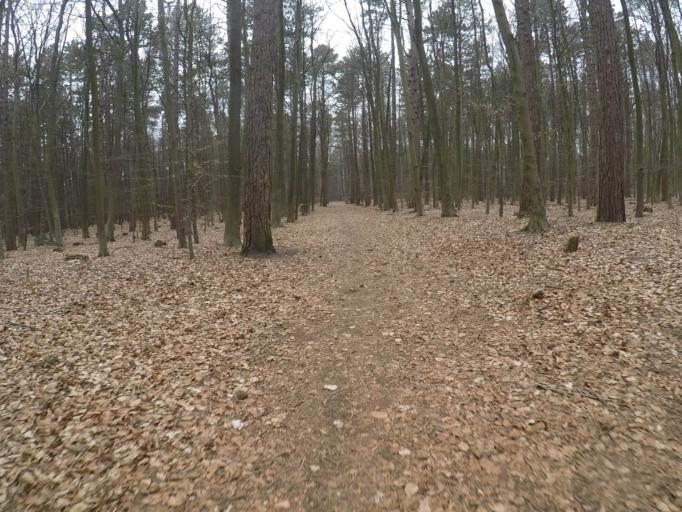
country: DE
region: Lower Saxony
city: Nordholz
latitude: 53.8173
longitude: 8.6508
